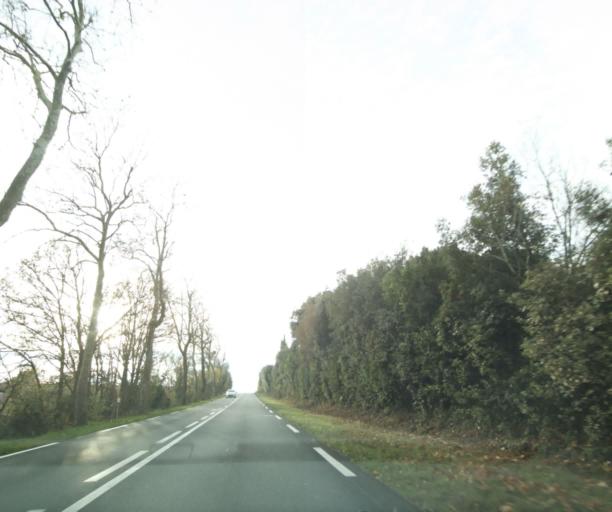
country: FR
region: Midi-Pyrenees
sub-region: Departement du Gers
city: Vic-Fezensac
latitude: 43.7524
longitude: 0.2860
